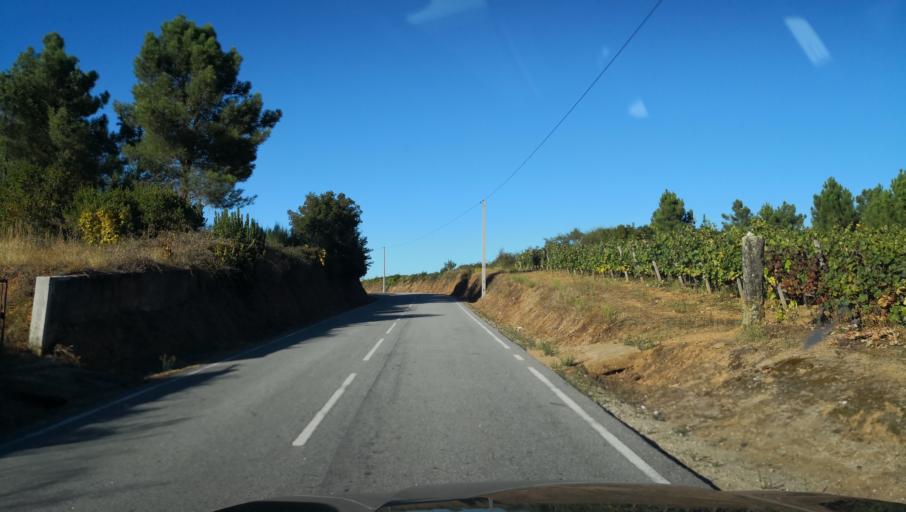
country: PT
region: Vila Real
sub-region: Sabrosa
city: Sabrosa
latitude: 41.2807
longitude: -7.5760
